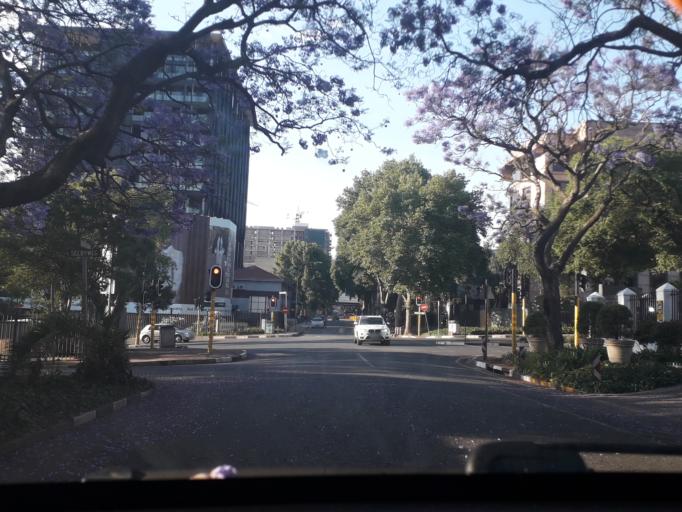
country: ZA
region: Gauteng
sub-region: City of Johannesburg Metropolitan Municipality
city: Johannesburg
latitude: -26.1497
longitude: 28.0413
